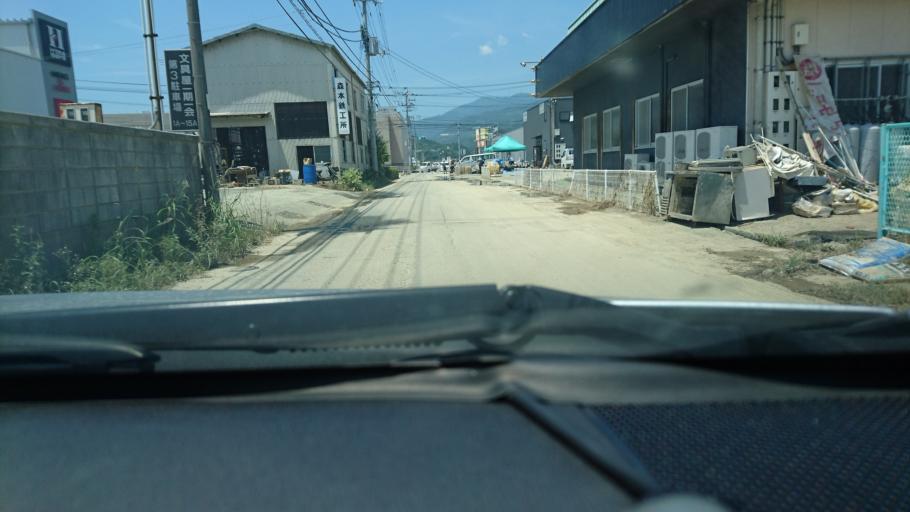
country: JP
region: Ehime
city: Ozu
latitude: 33.5283
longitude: 132.5692
